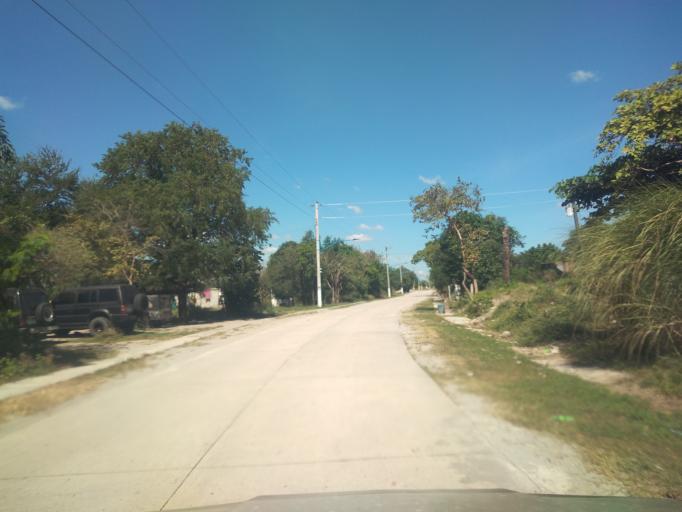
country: PH
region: Central Luzon
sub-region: Province of Pampanga
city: Balas
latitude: 15.0426
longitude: 120.6147
